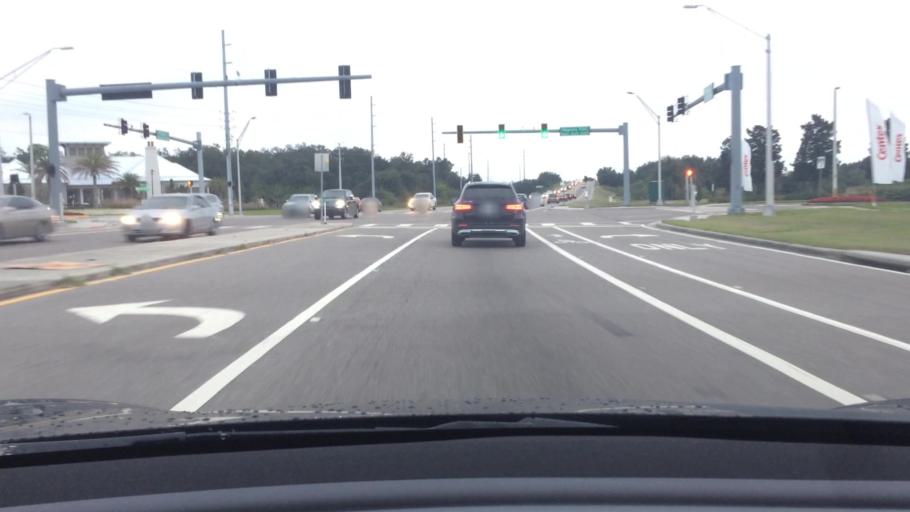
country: US
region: Florida
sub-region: Hillsborough County
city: Progress Village
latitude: 27.8983
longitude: -82.3524
